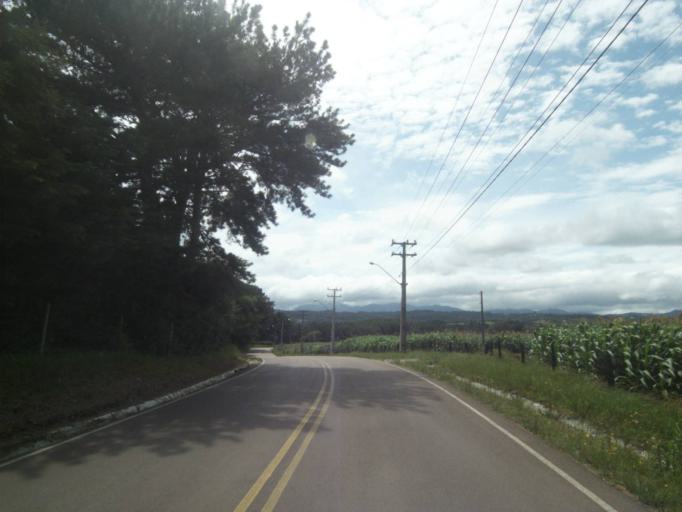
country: BR
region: Parana
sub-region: Campina Grande Do Sul
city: Campina Grande do Sul
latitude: -25.3126
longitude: -49.0337
